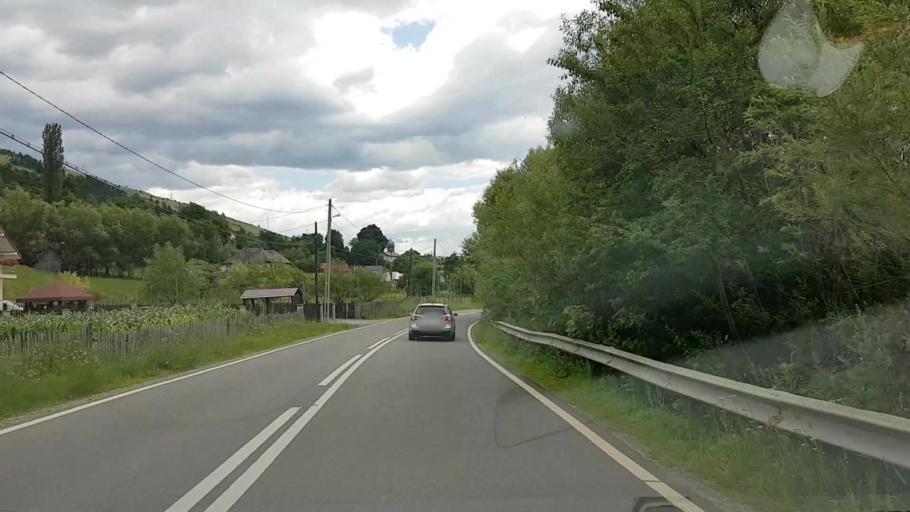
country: RO
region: Neamt
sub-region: Comuna Farcasa
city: Farcasa
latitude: 47.1692
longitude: 25.8015
